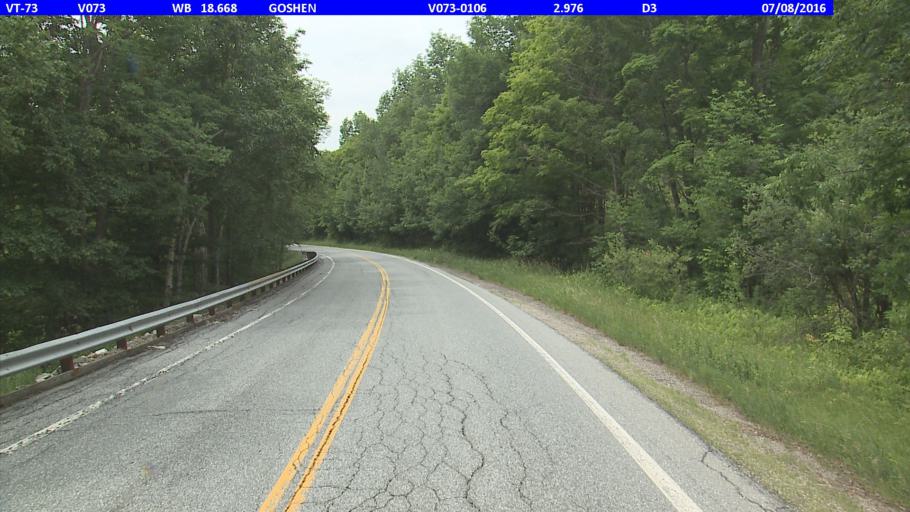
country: US
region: Vermont
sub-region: Rutland County
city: Brandon
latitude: 43.8428
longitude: -72.9747
